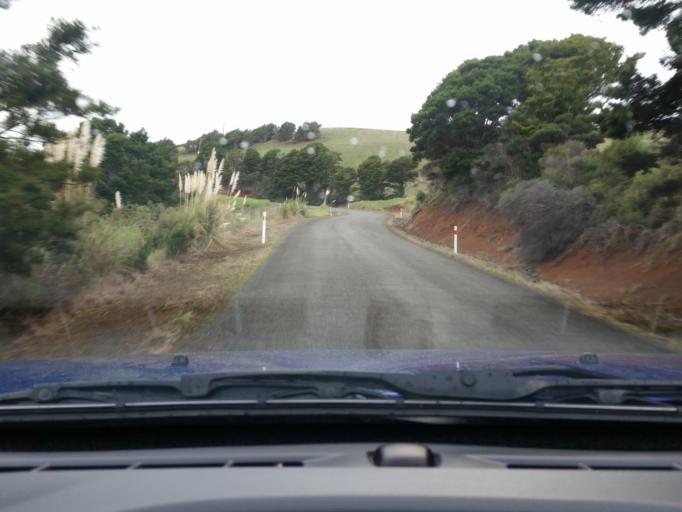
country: NZ
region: Northland
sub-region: Kaipara District
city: Dargaville
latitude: -35.7660
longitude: 173.6076
